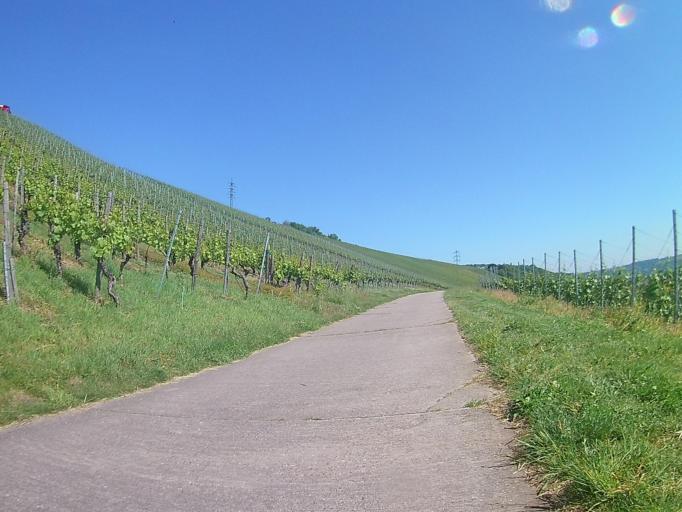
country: DE
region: Baden-Wuerttemberg
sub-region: Regierungsbezirk Stuttgart
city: Fellbach
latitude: 48.7741
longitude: 9.2623
